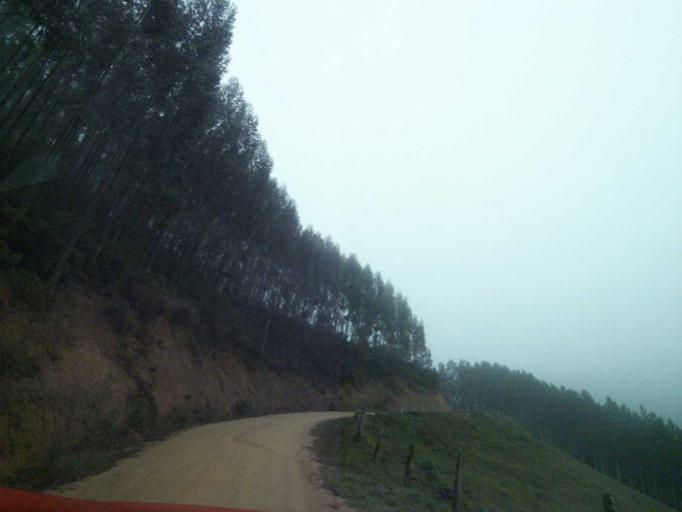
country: BR
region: Santa Catarina
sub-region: Anitapolis
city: Anitapolis
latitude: -27.9136
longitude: -49.0968
